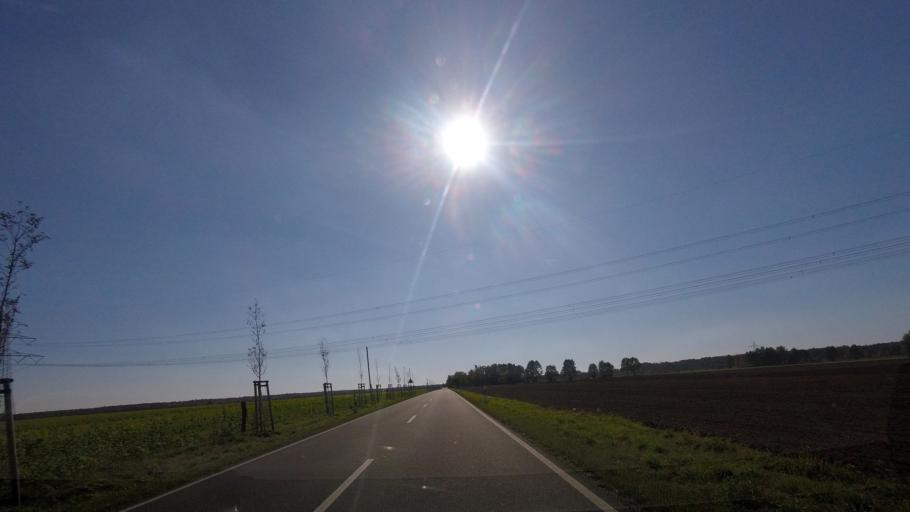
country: DE
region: Saxony-Anhalt
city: Zahna
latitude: 51.8757
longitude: 12.7875
